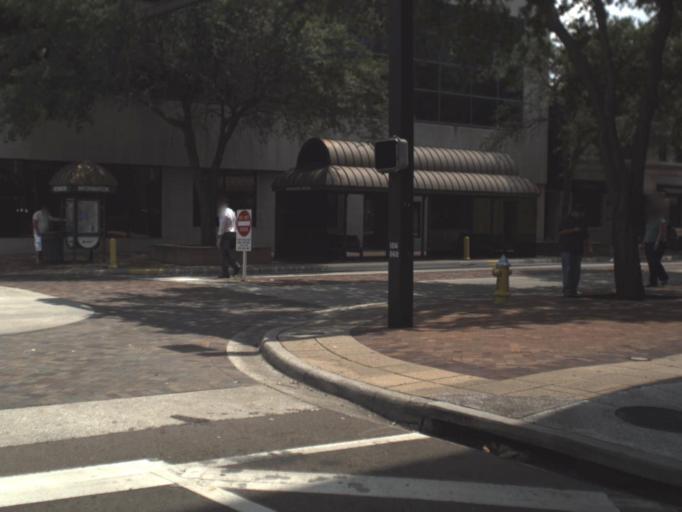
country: US
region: Florida
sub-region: Hillsborough County
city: Tampa
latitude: 27.9475
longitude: -82.4561
